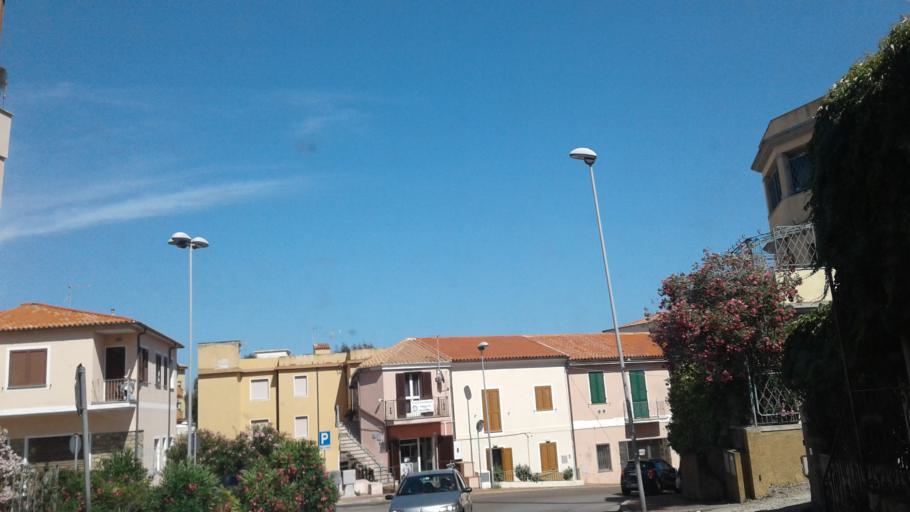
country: IT
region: Sardinia
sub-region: Provincia di Olbia-Tempio
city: La Maddalena
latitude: 41.2168
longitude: 9.4086
